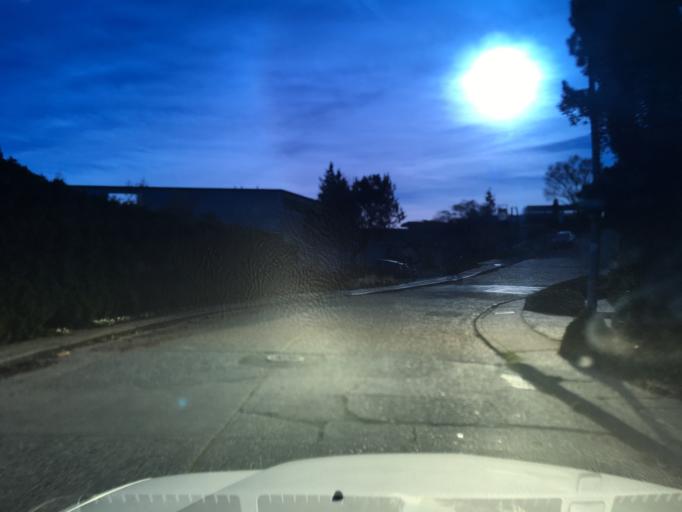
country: US
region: Washington
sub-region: King County
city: Inglewood-Finn Hill
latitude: 47.6813
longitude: -122.2670
